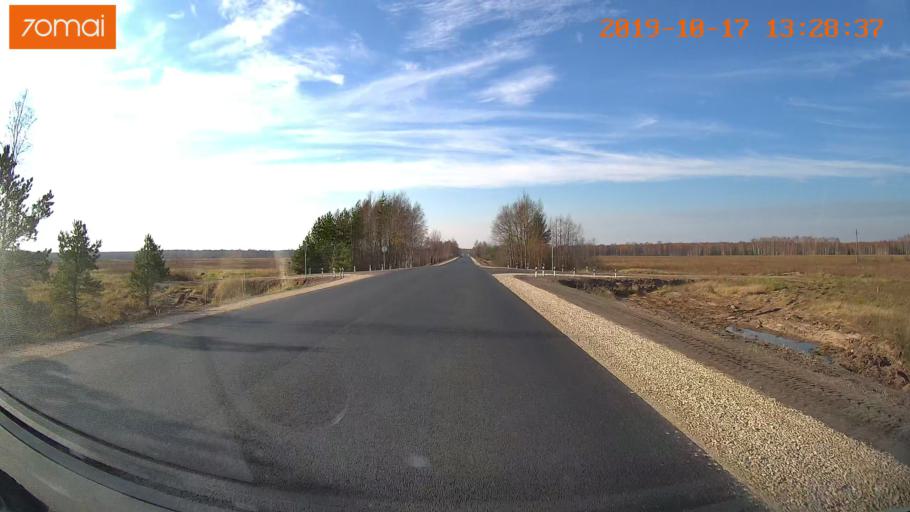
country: RU
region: Vladimir
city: Velikodvorskiy
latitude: 55.1168
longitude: 40.8637
